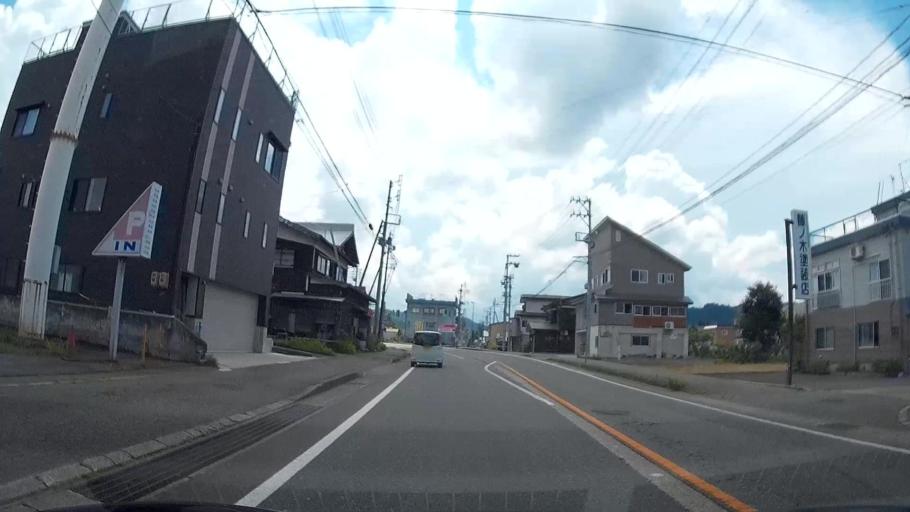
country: JP
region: Niigata
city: Tokamachi
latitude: 37.0201
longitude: 138.6563
